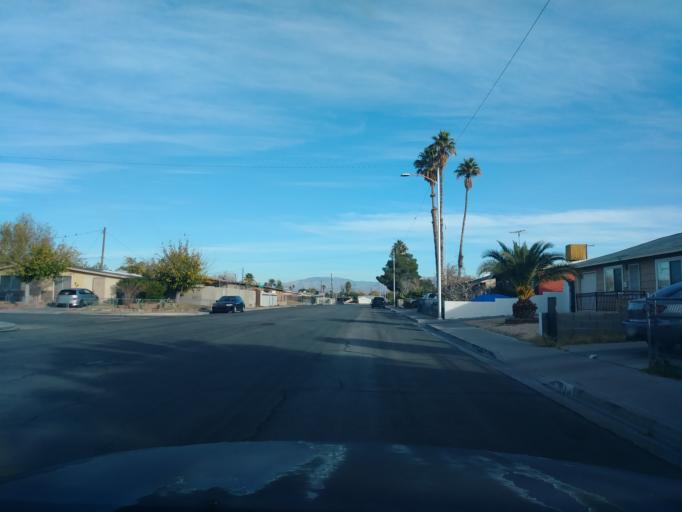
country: US
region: Nevada
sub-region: Clark County
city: Spring Valley
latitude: 36.1641
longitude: -115.2280
